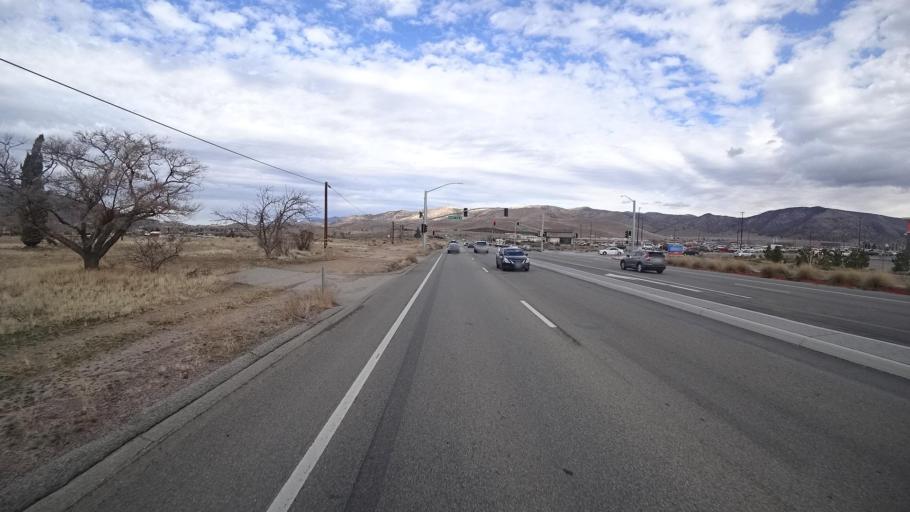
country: US
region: California
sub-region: Kern County
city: Tehachapi
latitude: 35.1290
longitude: -118.4675
